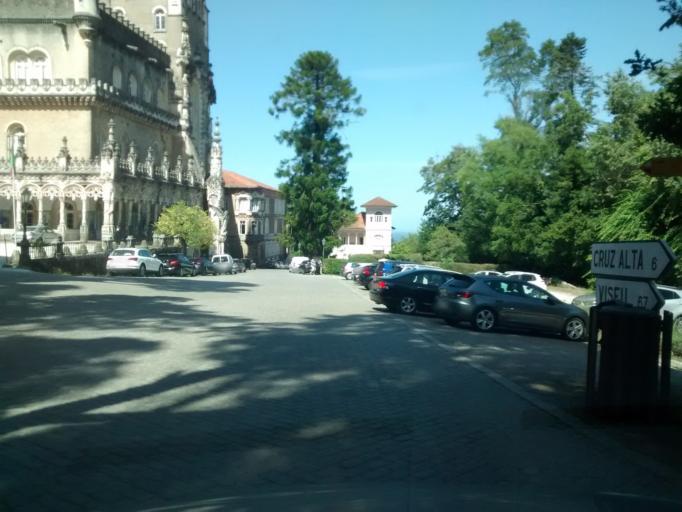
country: PT
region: Aveiro
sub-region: Mealhada
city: Pampilhosa do Botao
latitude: 40.3762
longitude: -8.3639
